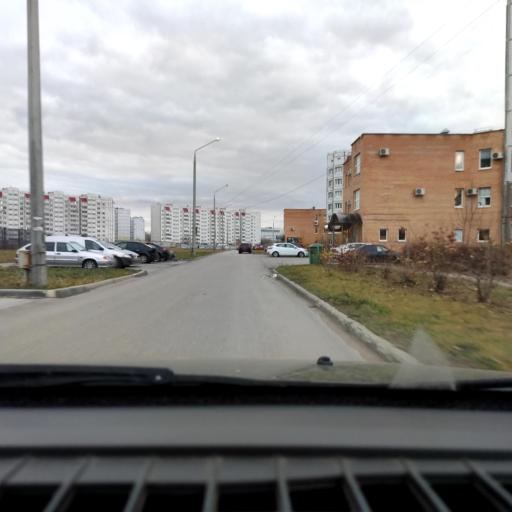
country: RU
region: Samara
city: Tol'yatti
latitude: 53.5278
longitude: 49.3397
